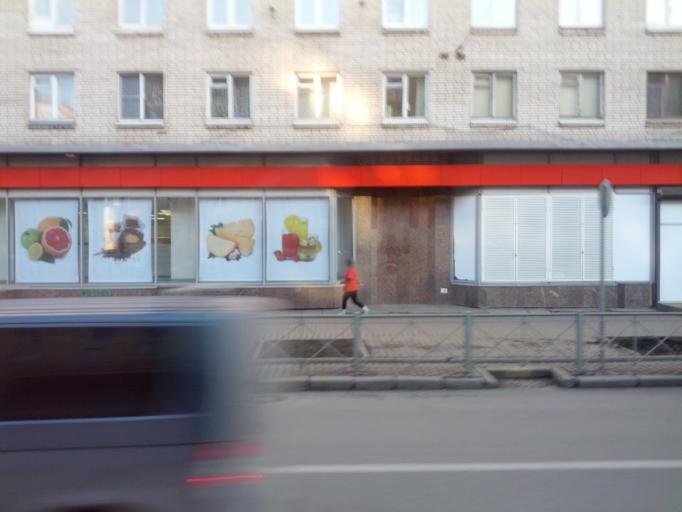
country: RU
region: Leningrad
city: Finlyandskiy
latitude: 59.9462
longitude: 30.4146
